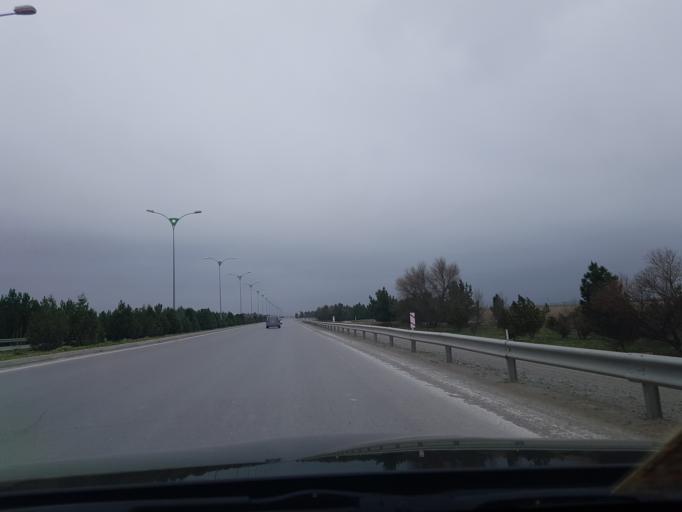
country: TM
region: Ahal
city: Abadan
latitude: 38.1473
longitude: 57.9871
